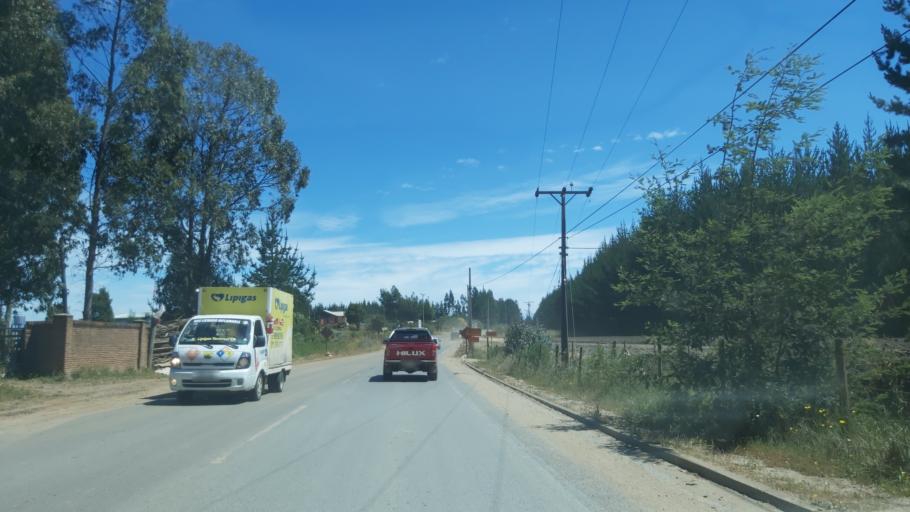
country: CL
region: Maule
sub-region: Provincia de Talca
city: Constitucion
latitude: -35.3911
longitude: -72.4247
